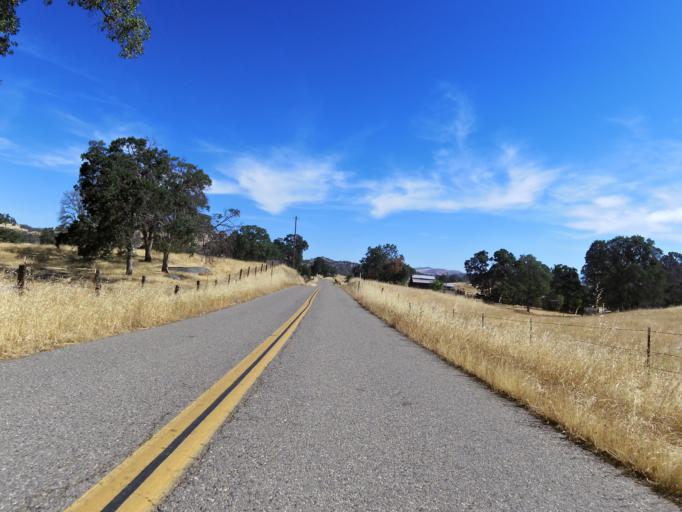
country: US
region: California
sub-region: Madera County
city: Yosemite Lakes
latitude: 37.2577
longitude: -119.9749
